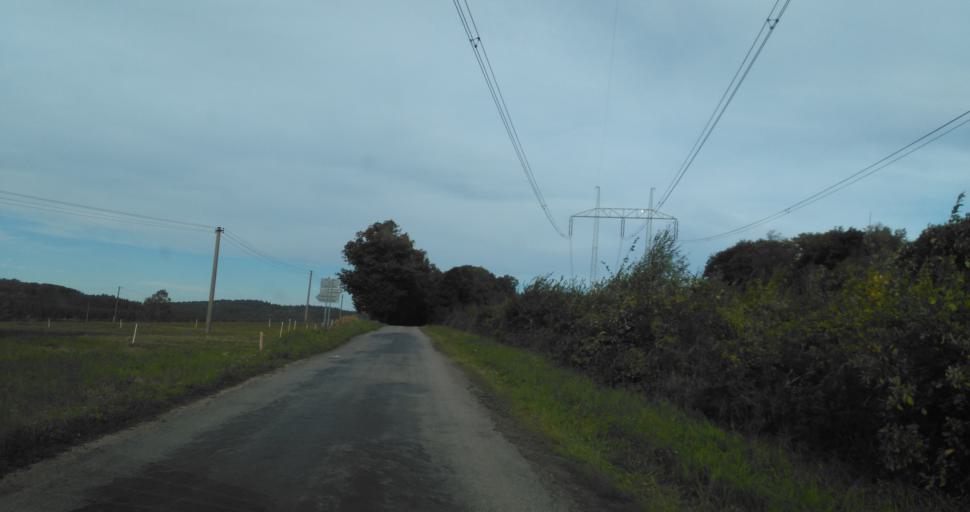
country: CZ
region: Plzensky
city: Zbiroh
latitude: 49.9180
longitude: 13.8242
